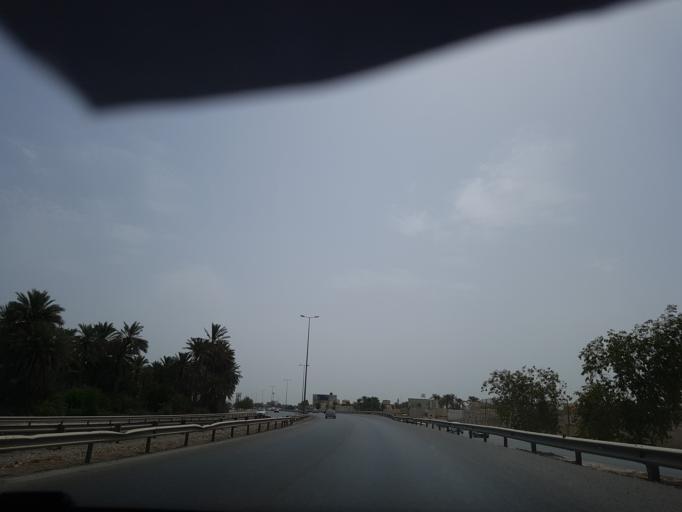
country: OM
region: Al Batinah
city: As Suwayq
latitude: 23.7535
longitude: 57.5671
